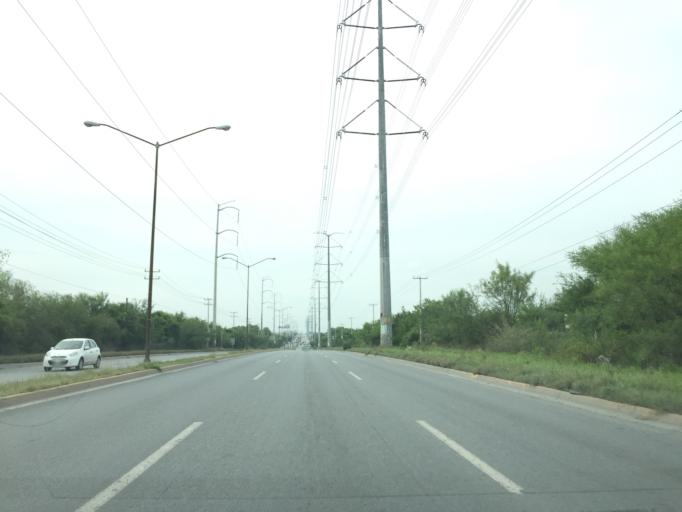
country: MX
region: Nuevo Leon
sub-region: Apodaca
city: Fraccionamiento Cosmopolis Octavo Sector
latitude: 25.7901
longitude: -100.2233
